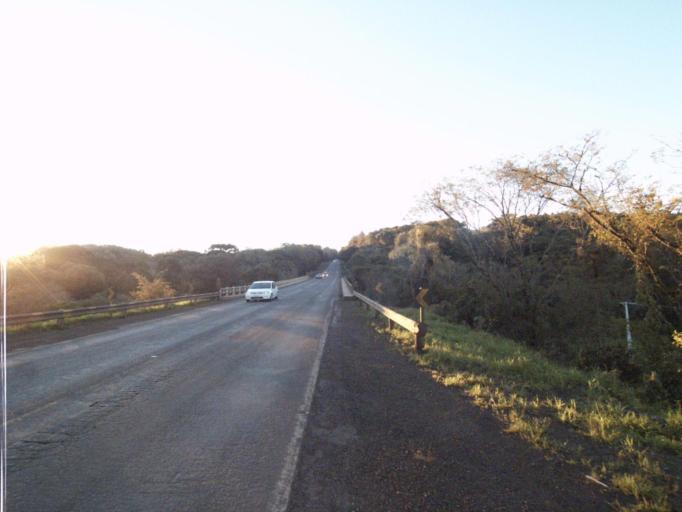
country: BR
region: Santa Catarina
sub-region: Sao Lourenco Do Oeste
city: Sao Lourenco dOeste
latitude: -26.7989
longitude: -53.1912
